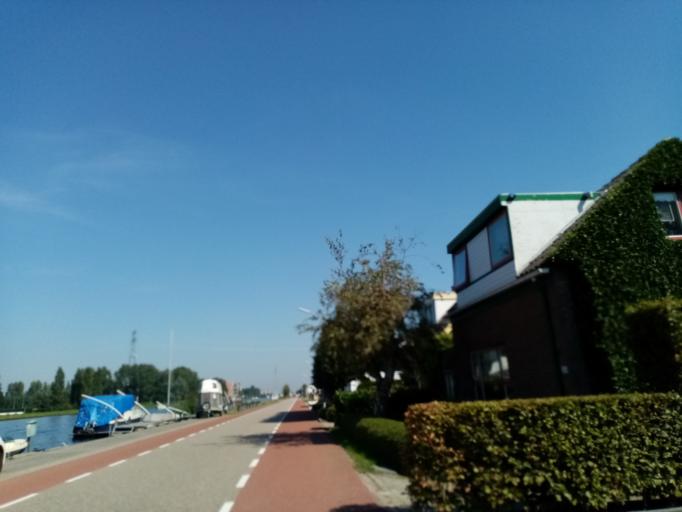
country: NL
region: South Holland
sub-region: Gemeente Lisse
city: Lisse
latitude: 52.2368
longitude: 4.5642
